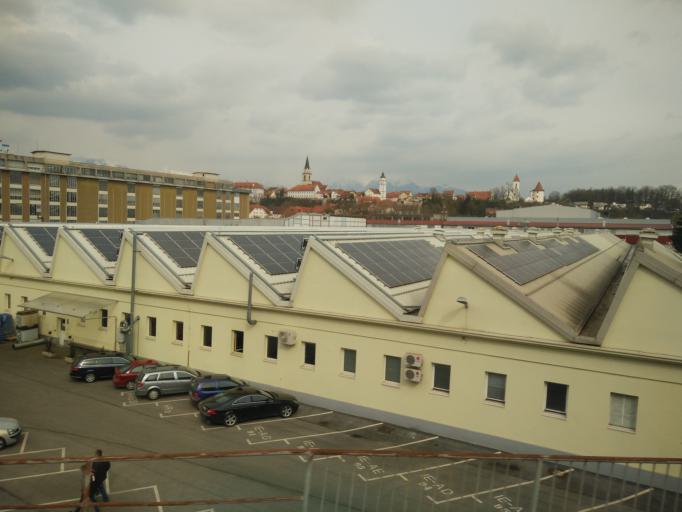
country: SI
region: Kranj
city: Kranj
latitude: 46.2352
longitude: 14.3492
